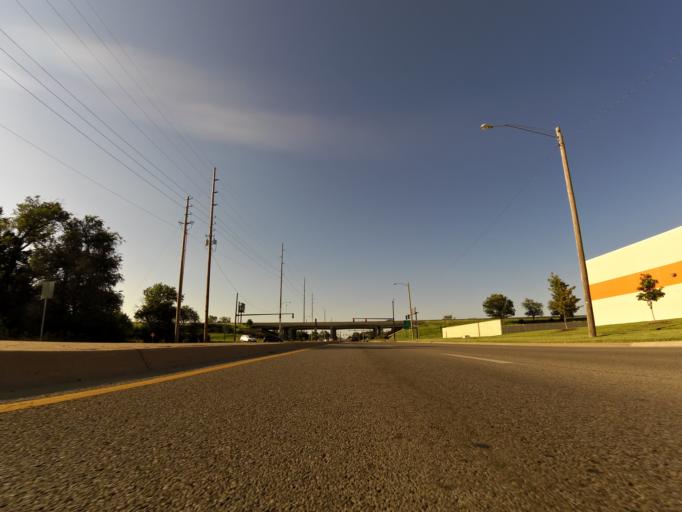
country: US
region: Kansas
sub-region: Sedgwick County
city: Bellaire
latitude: 37.7443
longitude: -97.2623
